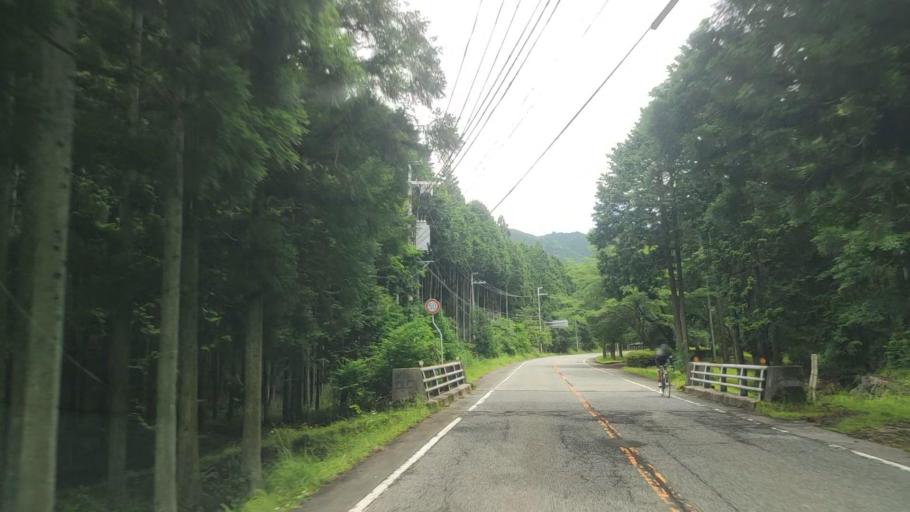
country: JP
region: Kyoto
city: Fukuchiyama
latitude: 35.2041
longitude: 134.9375
